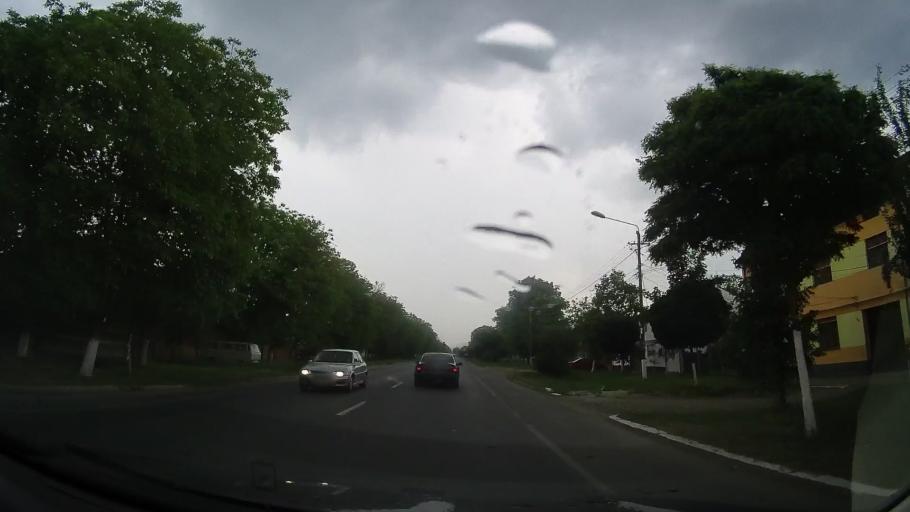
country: RO
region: Caras-Severin
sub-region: Municipiul Caransebes
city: Caransebes
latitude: 45.3979
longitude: 22.2254
